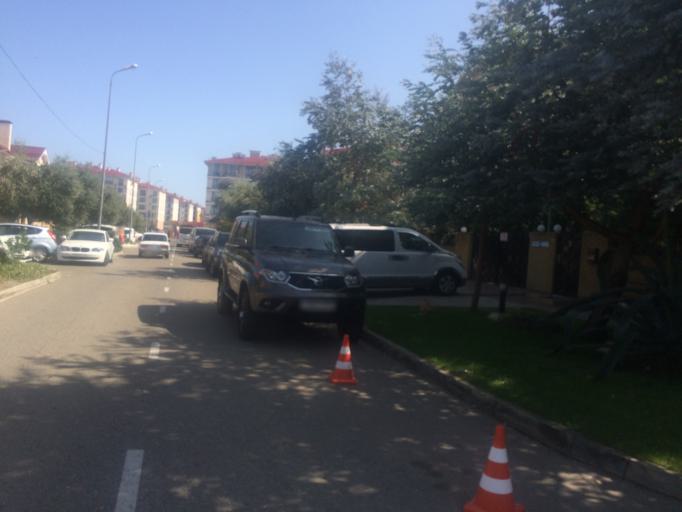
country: RU
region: Krasnodarskiy
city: Adler
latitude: 43.3980
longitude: 39.9735
